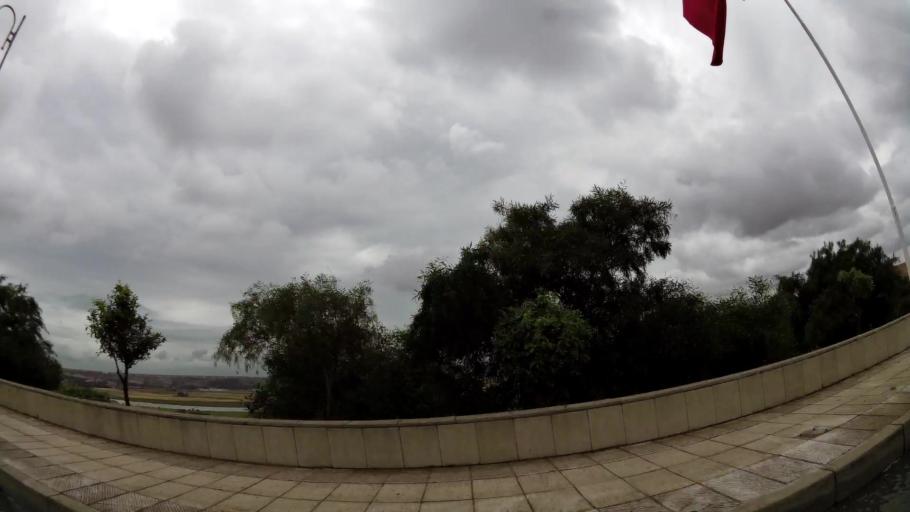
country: MA
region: Rabat-Sale-Zemmour-Zaer
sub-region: Rabat
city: Rabat
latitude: 34.0109
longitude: -6.8211
